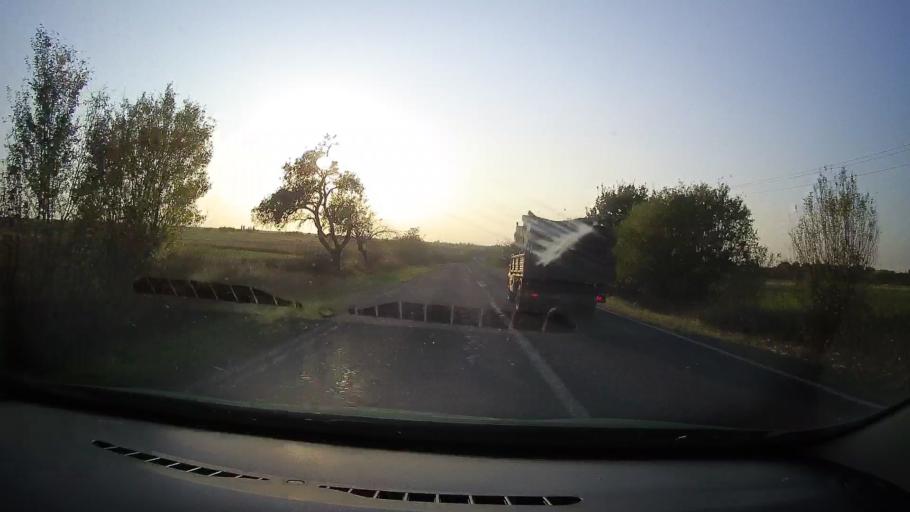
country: RO
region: Arad
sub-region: Comuna Barsa
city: Barsa
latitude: 46.3908
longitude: 22.0582
